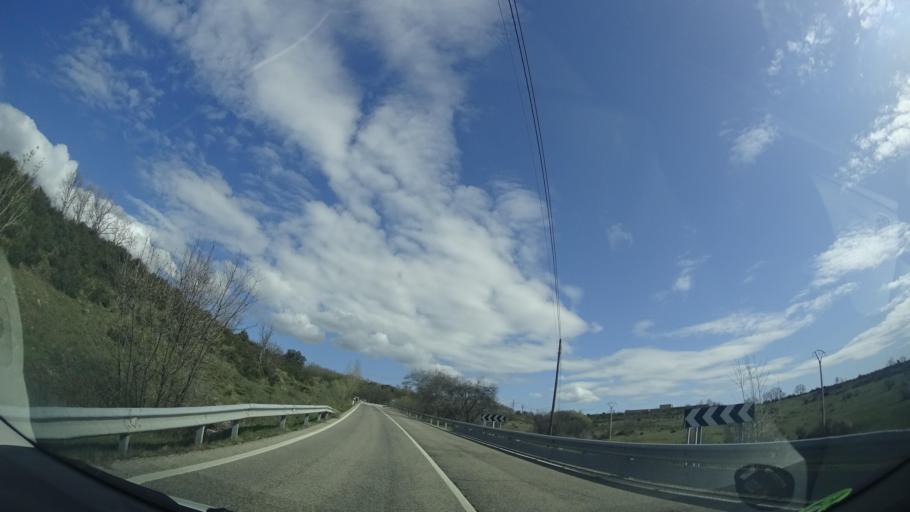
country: ES
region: Madrid
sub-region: Provincia de Madrid
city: Miraflores de la Sierra
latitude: 40.7726
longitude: -3.7791
